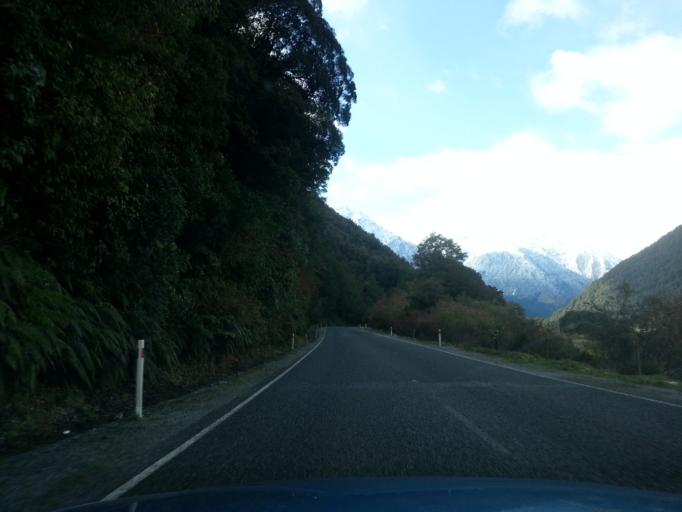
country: NZ
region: West Coast
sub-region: Grey District
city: Greymouth
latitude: -42.7805
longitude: 171.6125
